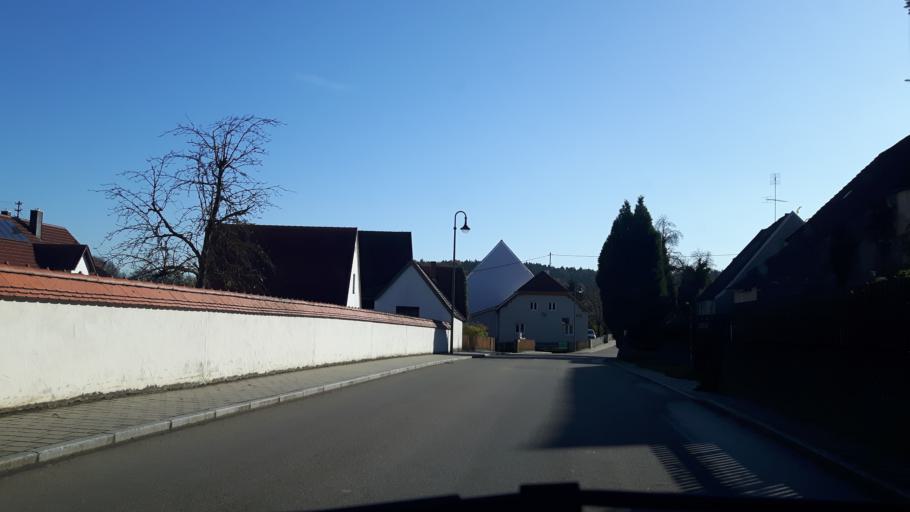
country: DE
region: Bavaria
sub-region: Swabia
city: Marxheim
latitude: 48.7789
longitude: 10.9547
